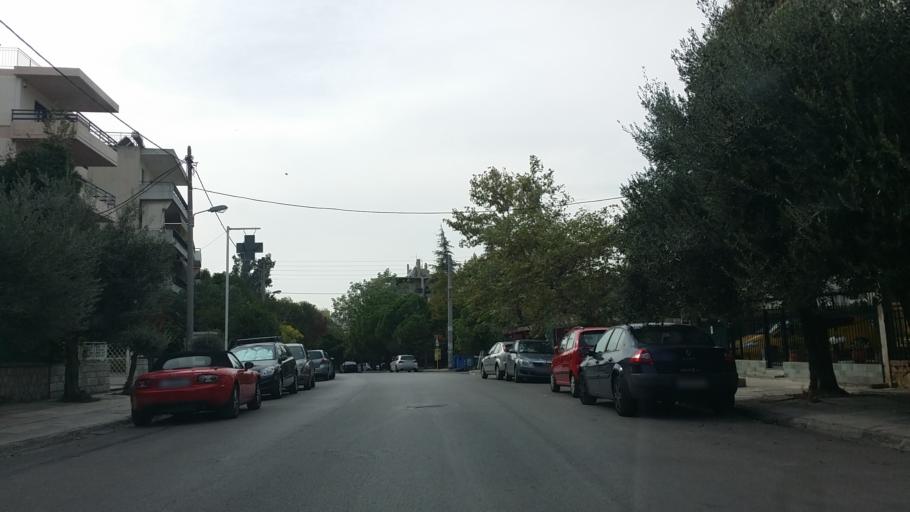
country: GR
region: Attica
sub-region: Nomarchia Athinas
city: Filothei
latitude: 38.0327
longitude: 23.7846
